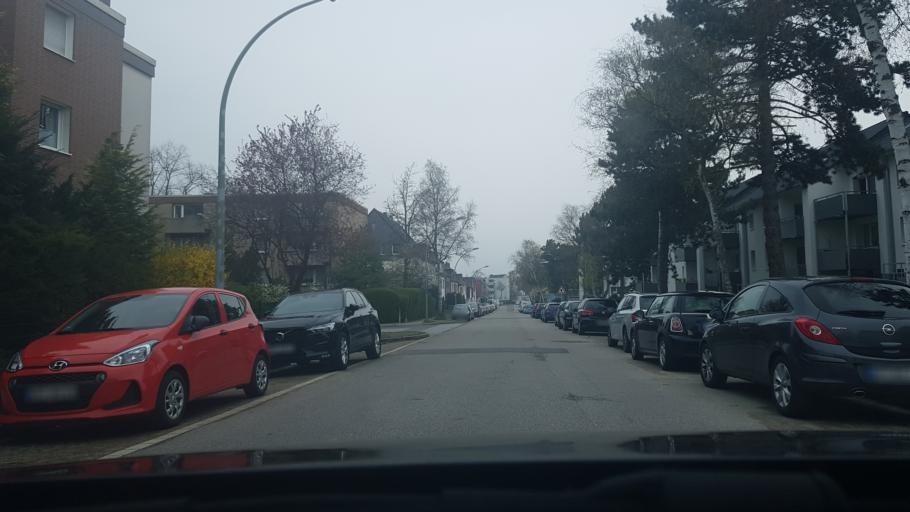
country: DE
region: North Rhine-Westphalia
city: Bochum-Hordel
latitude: 51.4677
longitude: 7.1540
